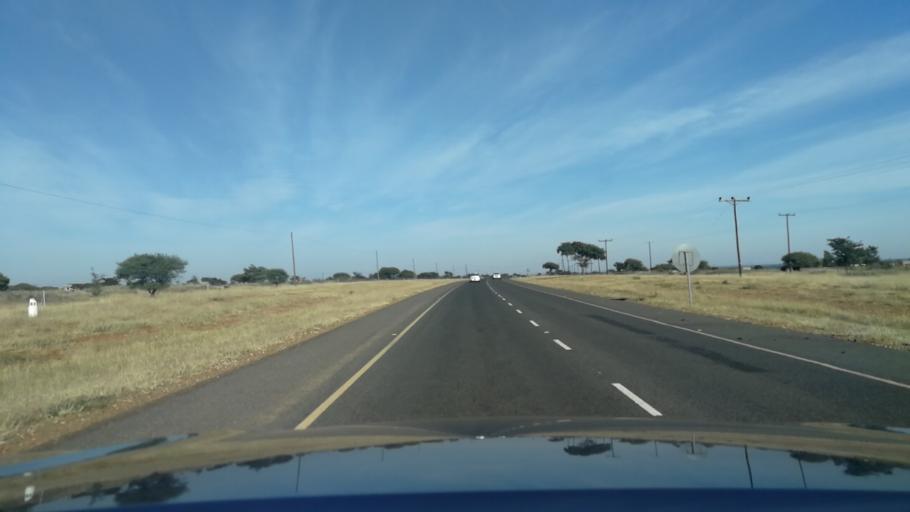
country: BW
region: South East
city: Janeng
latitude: -25.4715
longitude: 25.5317
